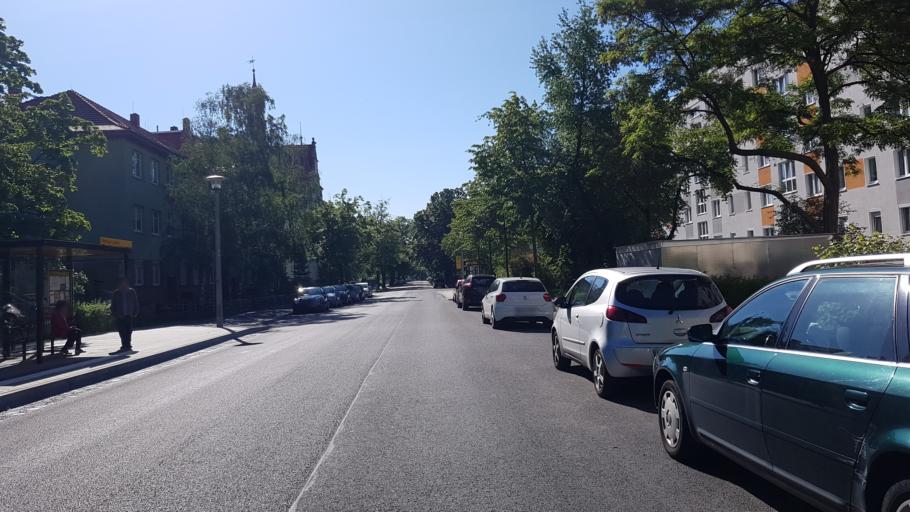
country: DE
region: Saxony
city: Heidenau
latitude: 51.0106
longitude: 13.8238
